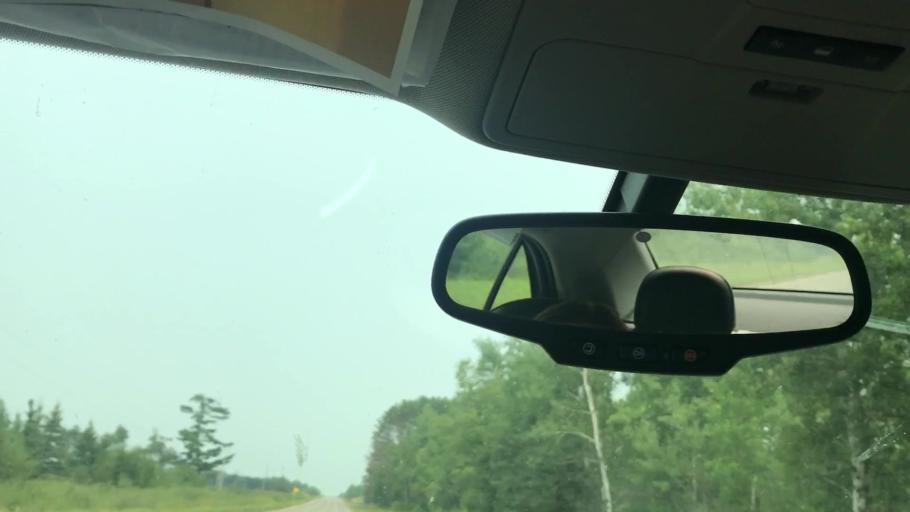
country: US
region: Minnesota
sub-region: Itasca County
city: Cohasset
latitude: 47.3729
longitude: -93.8803
